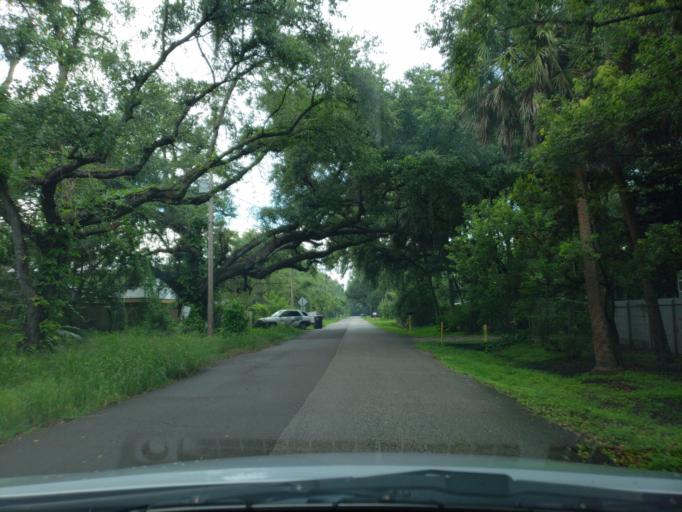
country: US
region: Florida
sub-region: Hillsborough County
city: Palm River-Clair Mel
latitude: 27.9298
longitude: -82.4076
